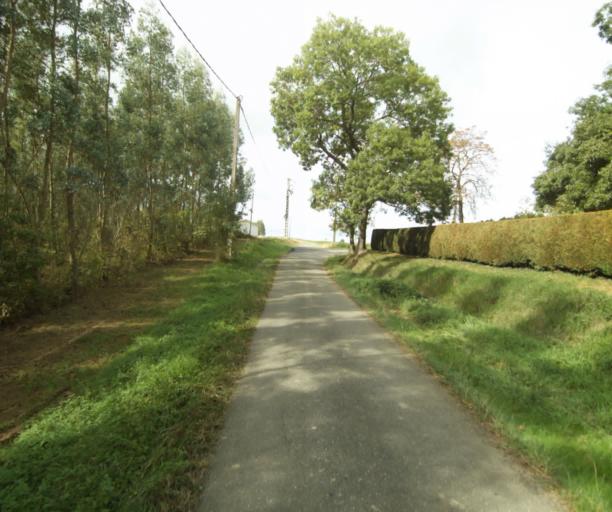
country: FR
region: Midi-Pyrenees
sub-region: Departement du Gers
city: Eauze
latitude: 43.8476
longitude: 0.0787
